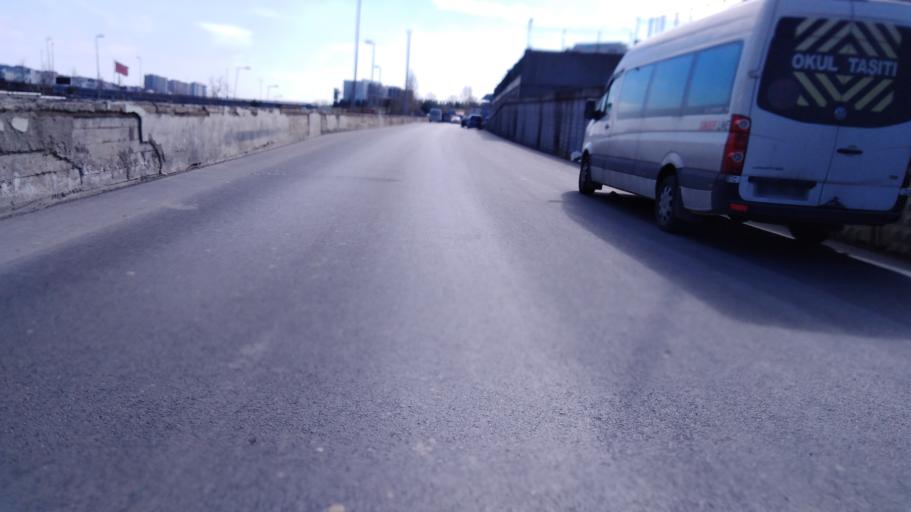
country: TR
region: Istanbul
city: Esenler
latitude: 41.0479
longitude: 28.8907
